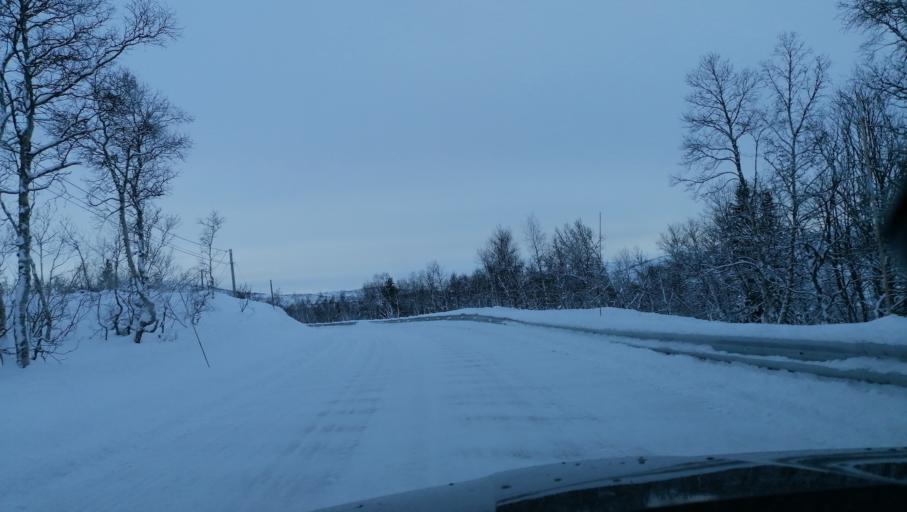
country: NO
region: Aust-Agder
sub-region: Bykle
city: Hovden
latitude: 59.6398
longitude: 7.4541
